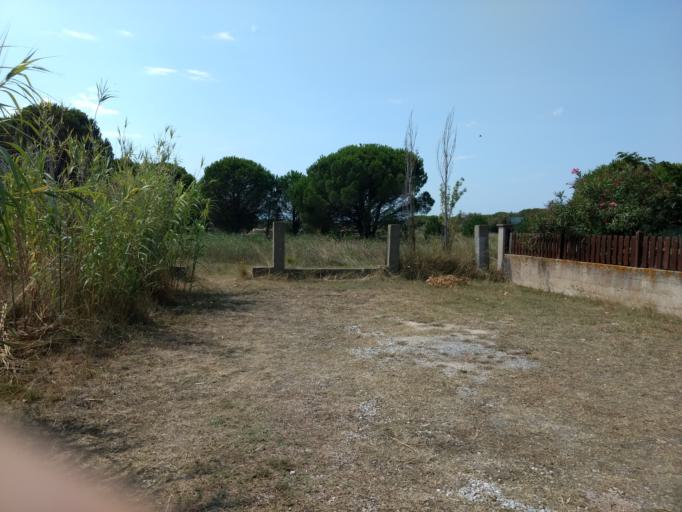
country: FR
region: Languedoc-Roussillon
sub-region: Departement des Pyrenees-Orientales
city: Le Barcares
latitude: 42.7878
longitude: 3.0285
